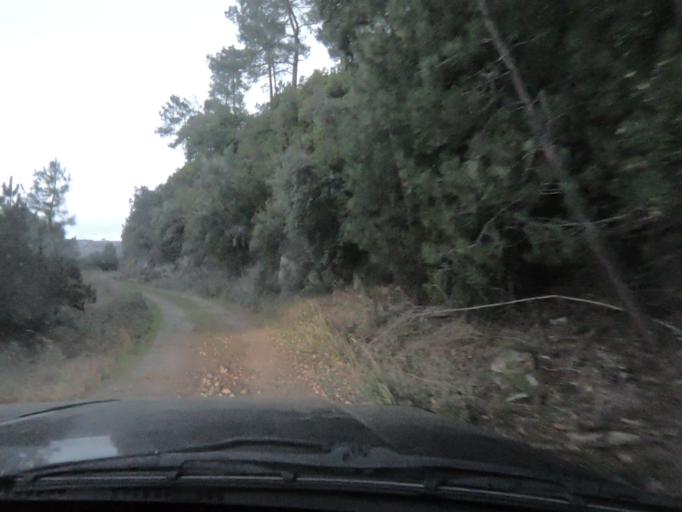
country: PT
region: Vila Real
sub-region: Vila Real
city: Vila Real
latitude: 41.2613
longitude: -7.7450
